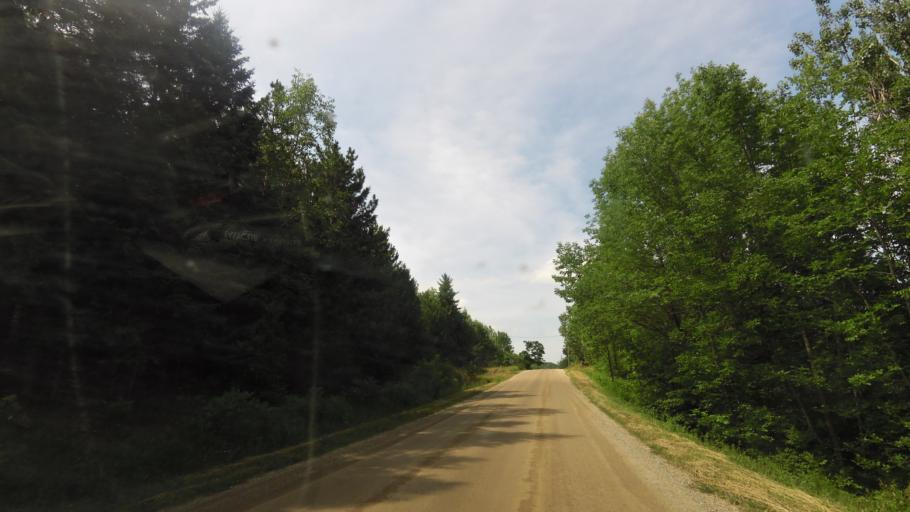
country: CA
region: Ontario
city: Orangeville
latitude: 43.9983
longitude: -80.0492
